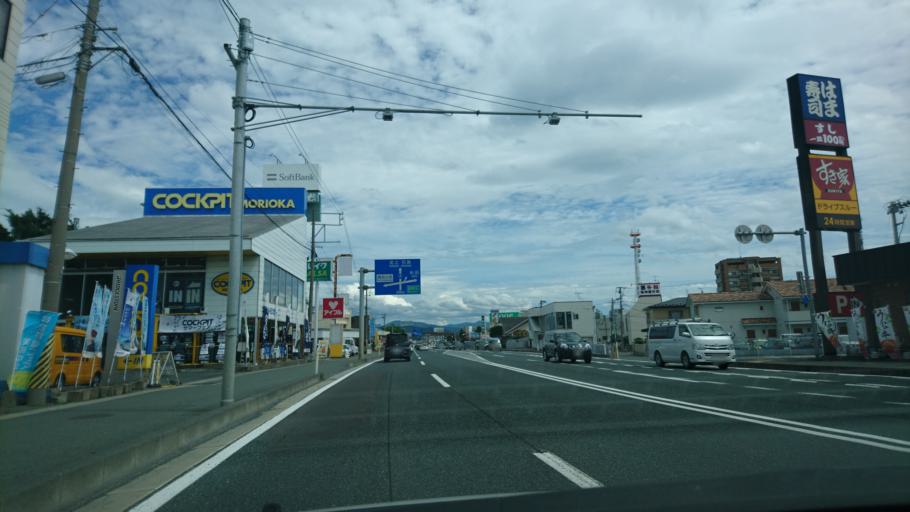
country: JP
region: Iwate
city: Morioka-shi
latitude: 39.7223
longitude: 141.1365
